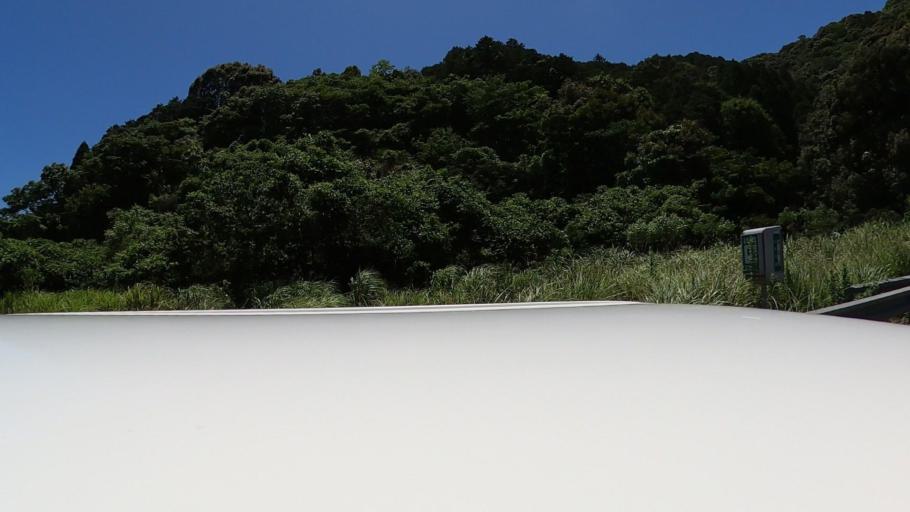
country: JP
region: Miyazaki
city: Nobeoka
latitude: 32.5459
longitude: 131.6460
